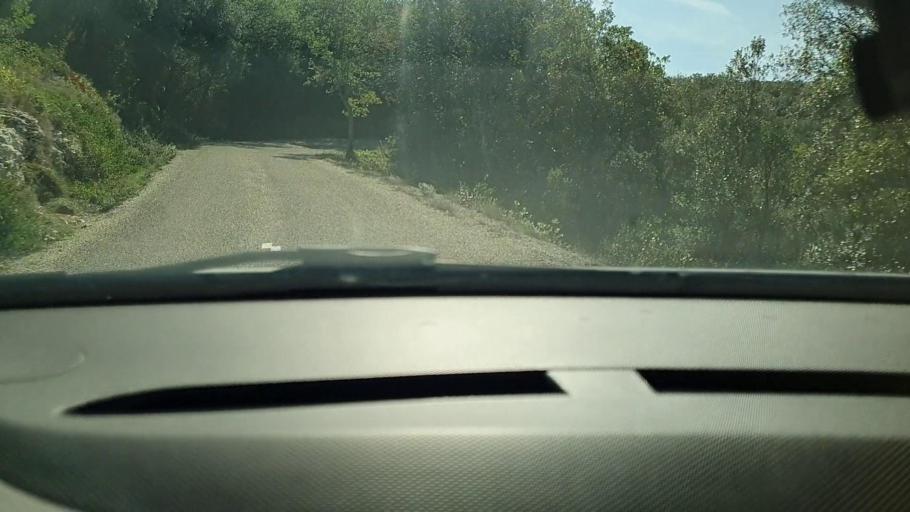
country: FR
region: Languedoc-Roussillon
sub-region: Departement du Gard
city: Barjac
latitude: 44.2005
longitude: 4.3129
